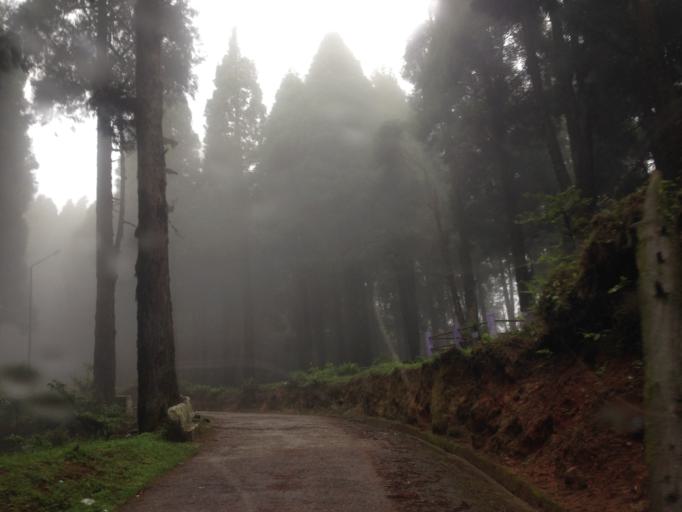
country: IN
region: West Bengal
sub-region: Darjiling
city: Darjiling
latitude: 26.9955
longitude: 88.1649
